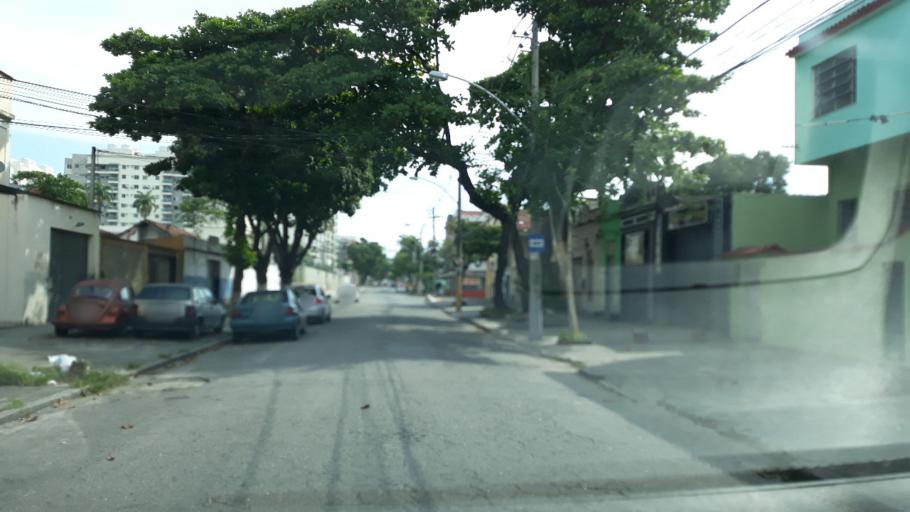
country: BR
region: Rio de Janeiro
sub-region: Duque De Caxias
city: Duque de Caxias
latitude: -22.8349
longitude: -43.2750
